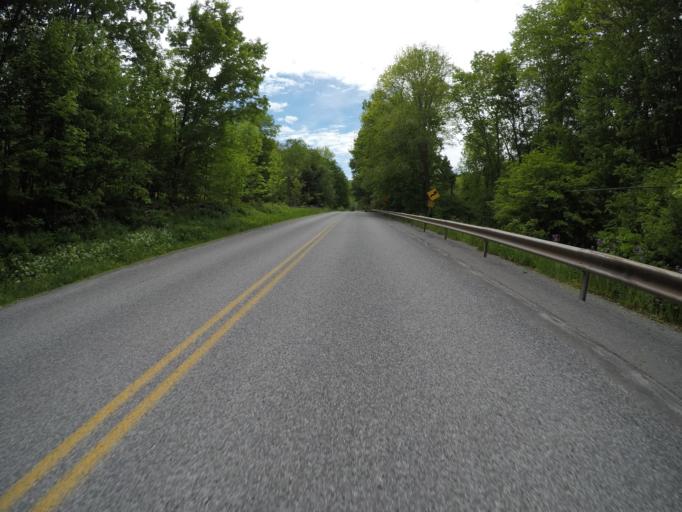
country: US
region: New York
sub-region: Delaware County
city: Stamford
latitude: 42.2146
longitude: -74.5692
